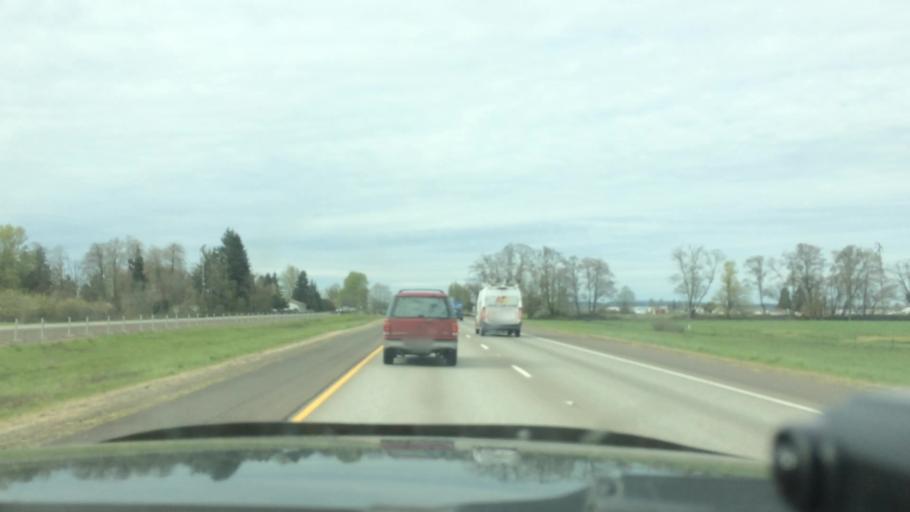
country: US
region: Oregon
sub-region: Linn County
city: Albany
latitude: 44.6040
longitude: -123.0619
